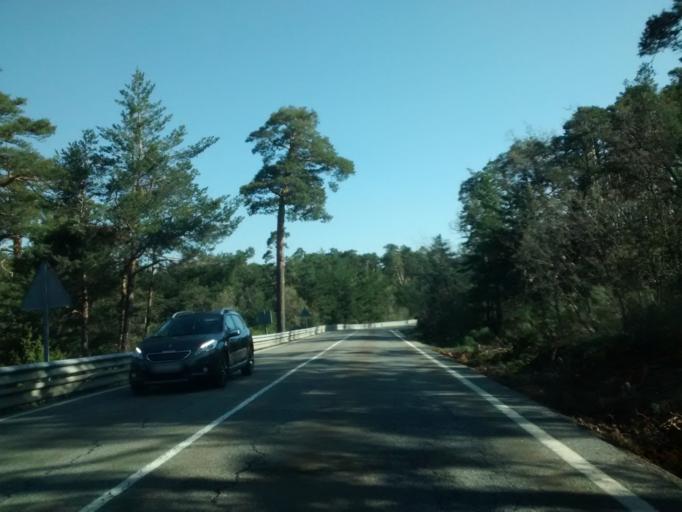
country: ES
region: Castille and Leon
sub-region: Provincia de Segovia
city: San Ildefonso
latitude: 40.8559
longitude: -4.0267
